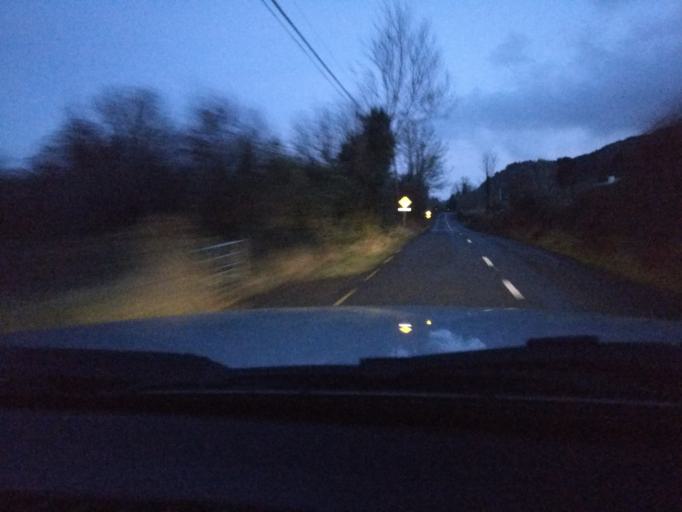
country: GB
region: Northern Ireland
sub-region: Down District
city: Warrenpoint
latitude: 54.0712
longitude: -6.2329
